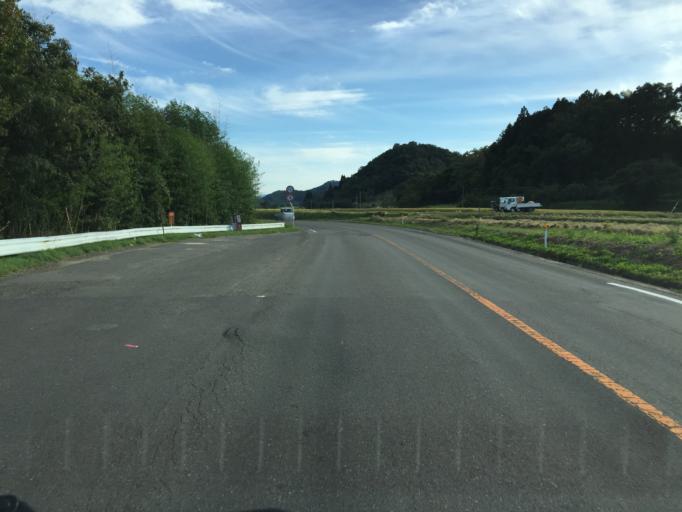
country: JP
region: Fukushima
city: Yanagawamachi-saiwaicho
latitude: 37.8416
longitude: 140.6145
